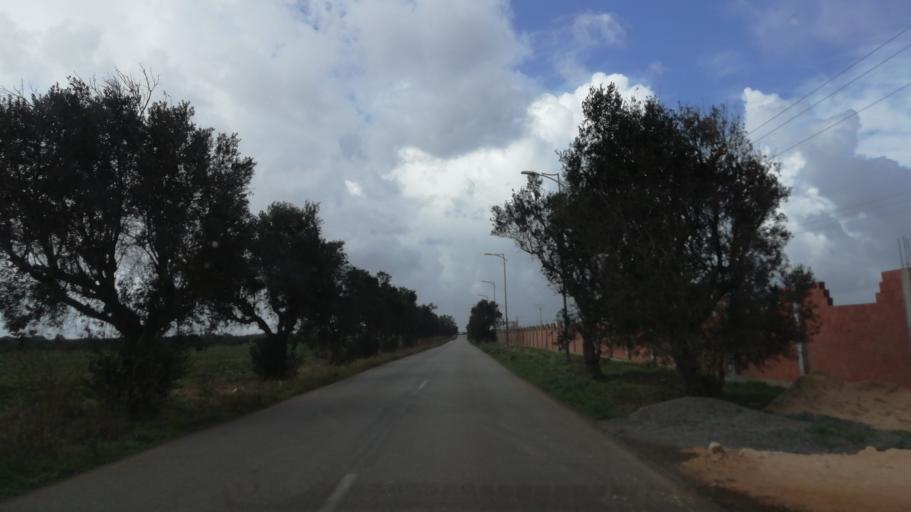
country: DZ
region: Oran
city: Sidi ech Chahmi
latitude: 35.6224
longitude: -0.5611
